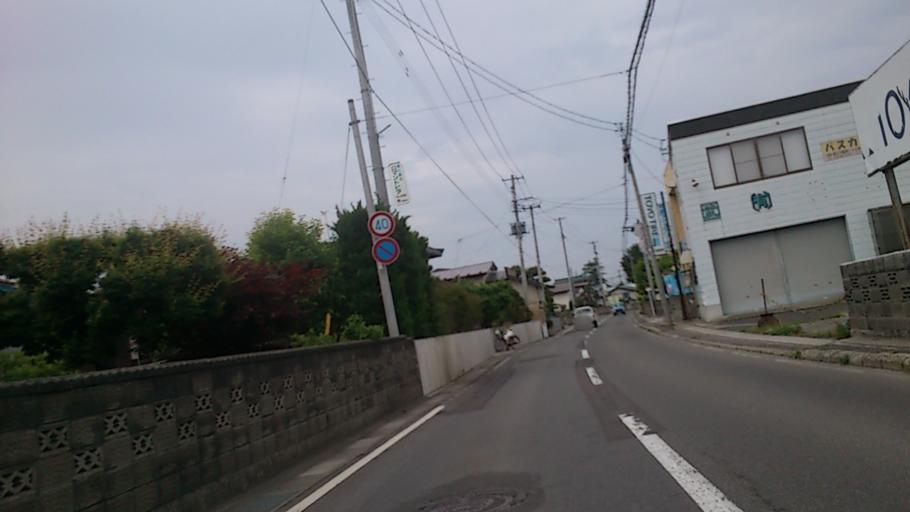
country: JP
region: Aomori
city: Hirosaki
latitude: 40.5928
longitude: 140.4320
